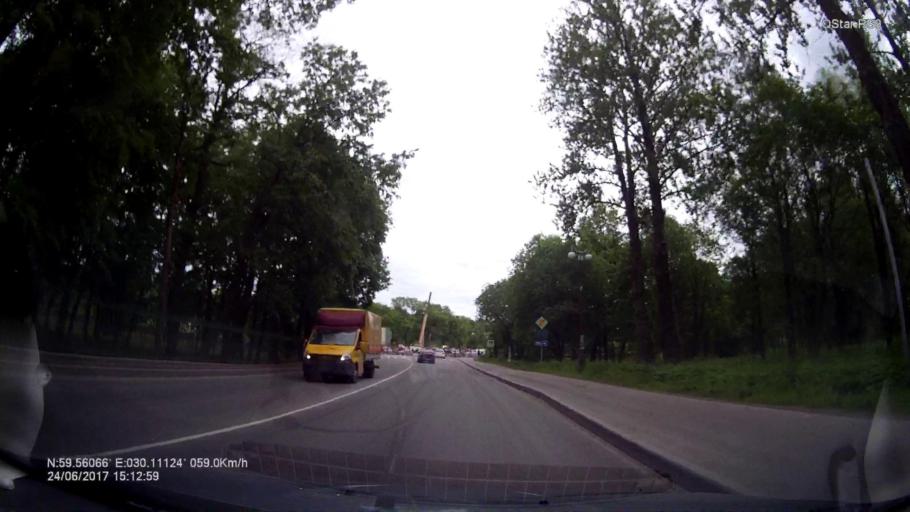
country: RU
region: Leningrad
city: Gatchina
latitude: 59.5605
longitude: 30.1115
